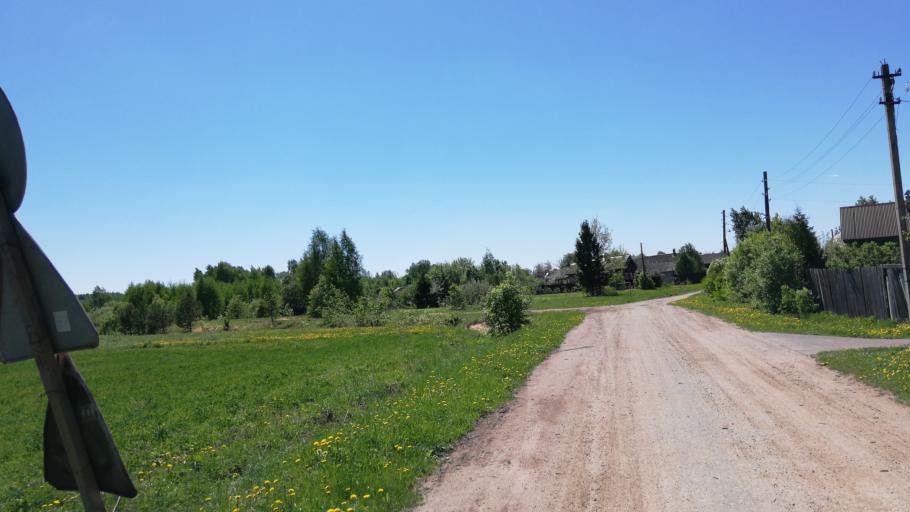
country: RU
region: Ivanovo
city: Pistsovo
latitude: 57.1188
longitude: 40.5977
